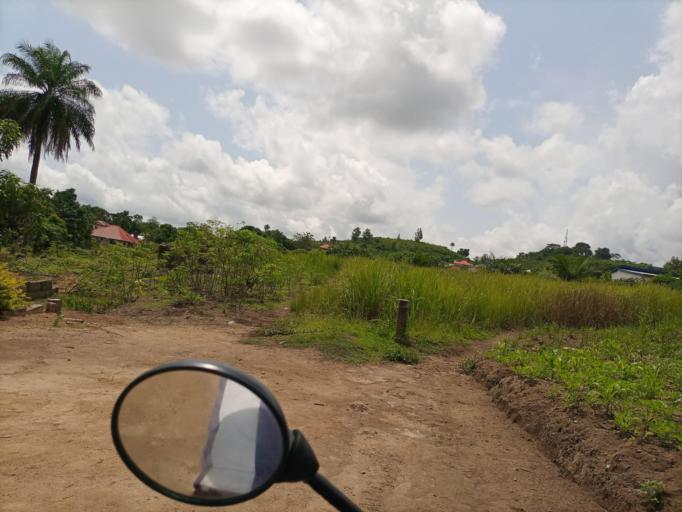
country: SL
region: Southern Province
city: Bo
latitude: 7.9778
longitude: -11.7658
